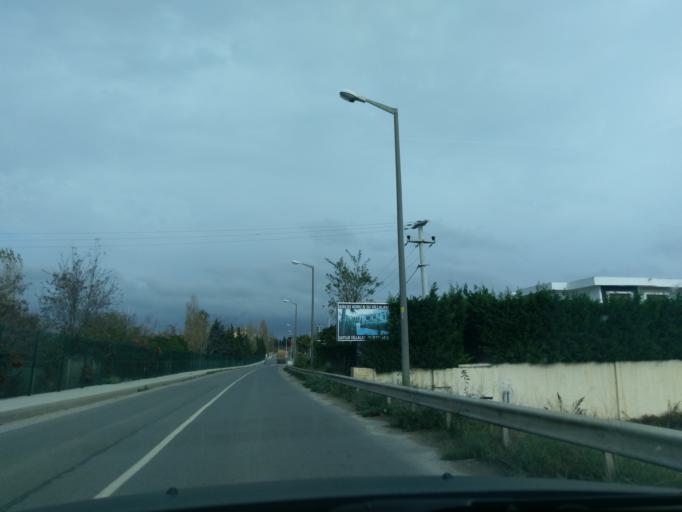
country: TR
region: Istanbul
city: Ortakoy
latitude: 41.0796
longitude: 28.3726
